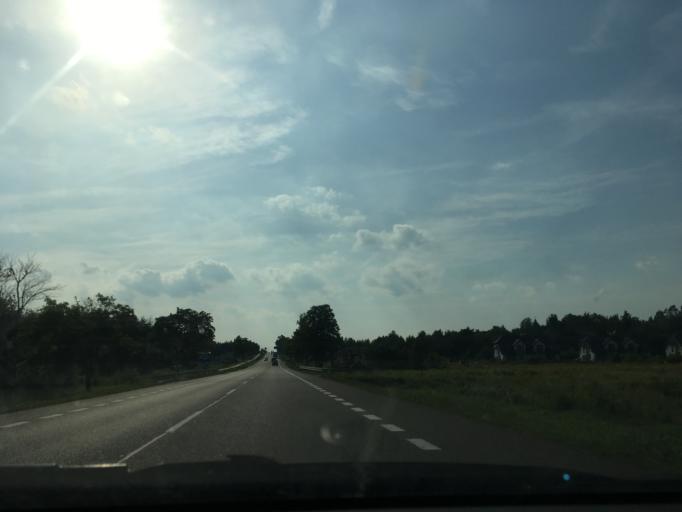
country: PL
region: Podlasie
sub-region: Powiat bialostocki
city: Wasilkow
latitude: 53.1254
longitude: 23.2716
